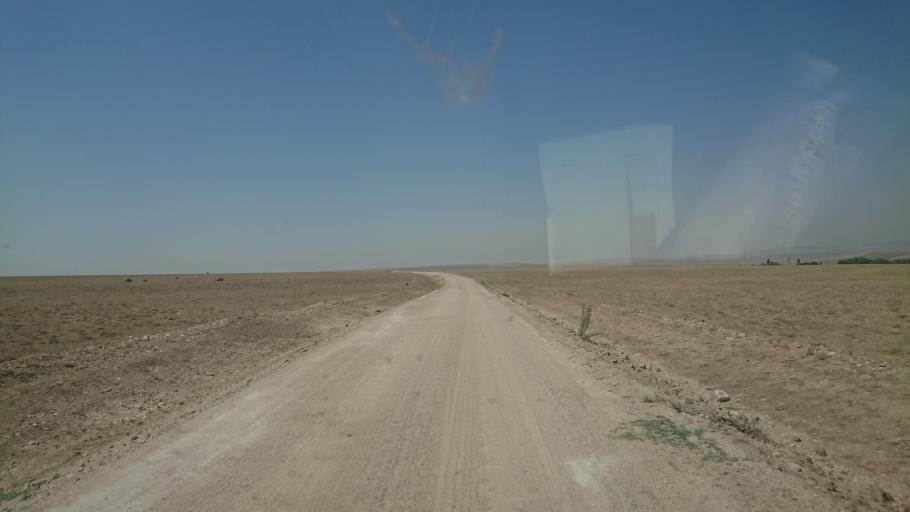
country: TR
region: Aksaray
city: Agacoren
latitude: 38.7480
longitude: 33.9042
